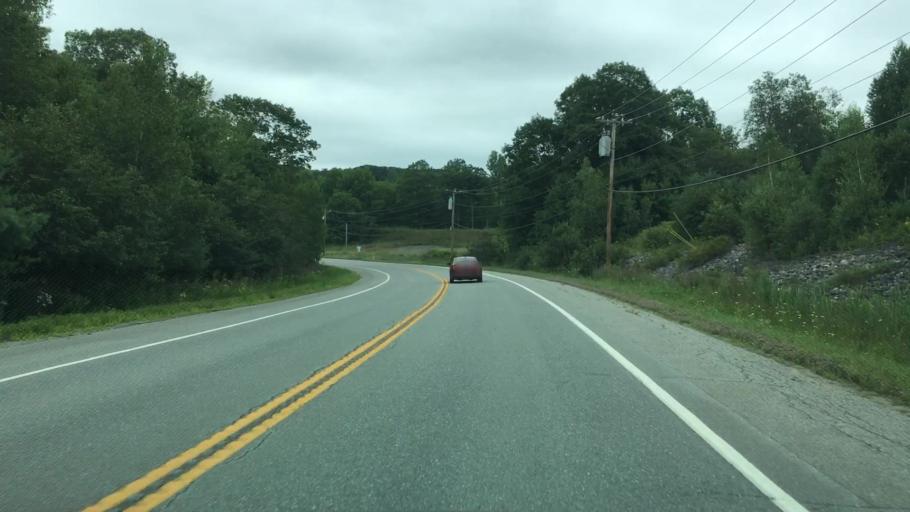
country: US
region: Maine
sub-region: Waldo County
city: Frankfort
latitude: 44.6234
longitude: -68.8693
